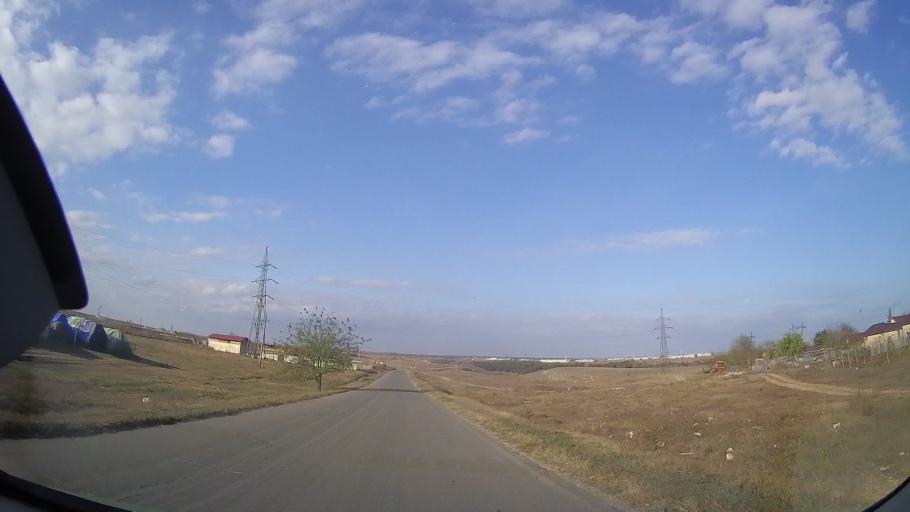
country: RO
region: Constanta
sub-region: Comuna Limanu
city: Limanu
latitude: 43.8019
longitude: 28.5220
